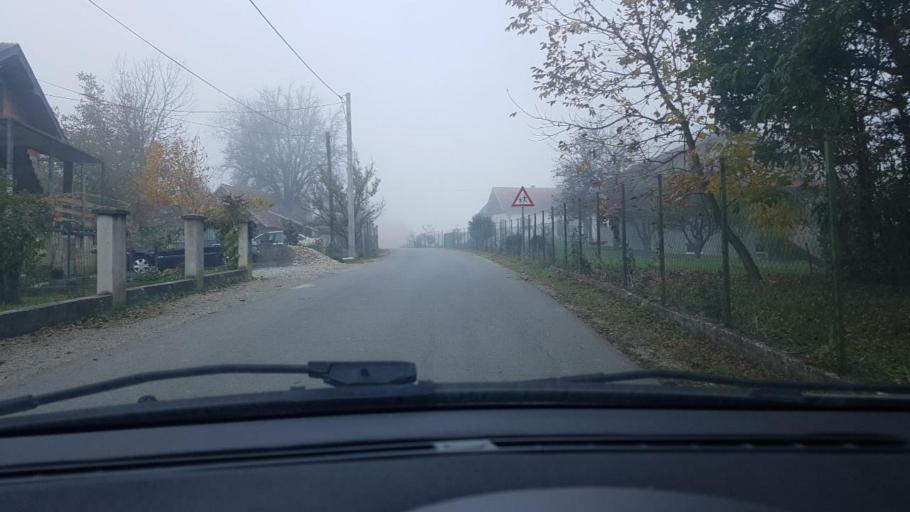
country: HR
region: Krapinsko-Zagorska
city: Mihovljan
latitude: 46.1527
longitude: 15.9901
